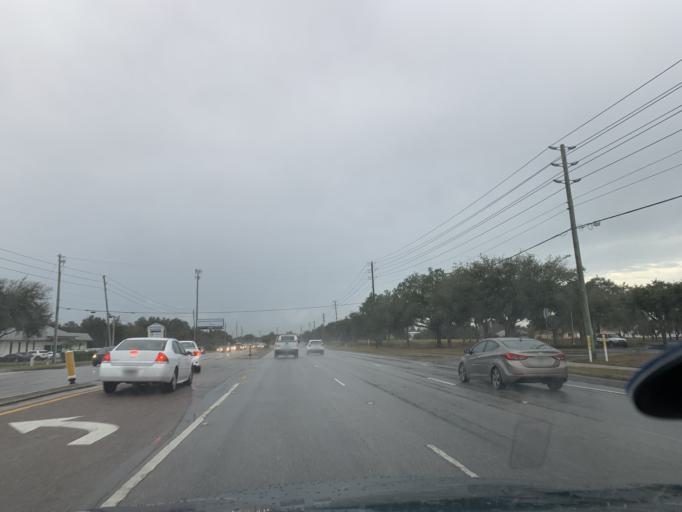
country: US
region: Florida
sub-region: Pasco County
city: Jasmine Estates
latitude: 28.2979
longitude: -82.6727
